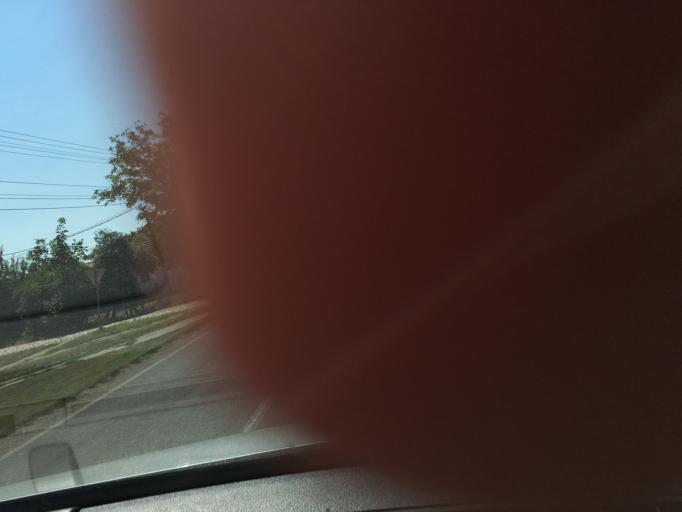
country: RS
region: Central Serbia
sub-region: Belgrade
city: Grocka
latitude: 44.7645
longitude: 20.7326
